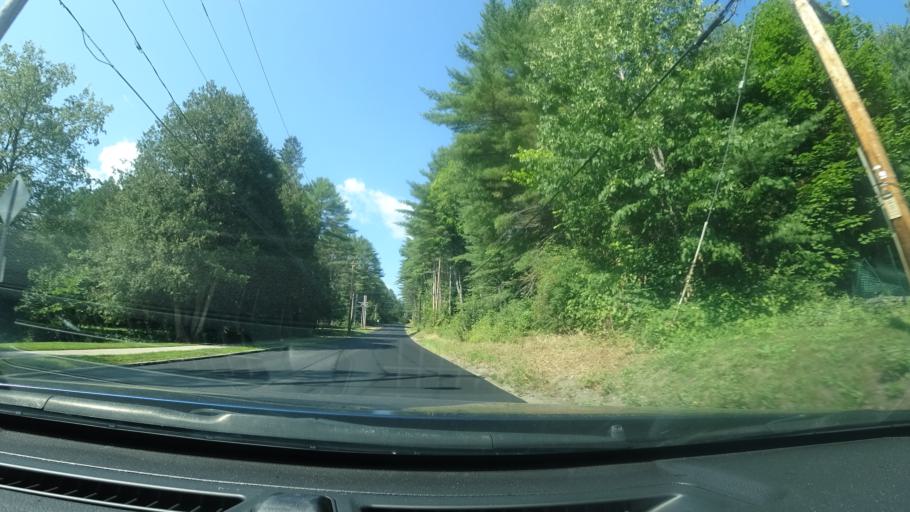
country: US
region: New York
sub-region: Warren County
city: Warrensburg
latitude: 43.6535
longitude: -73.8076
